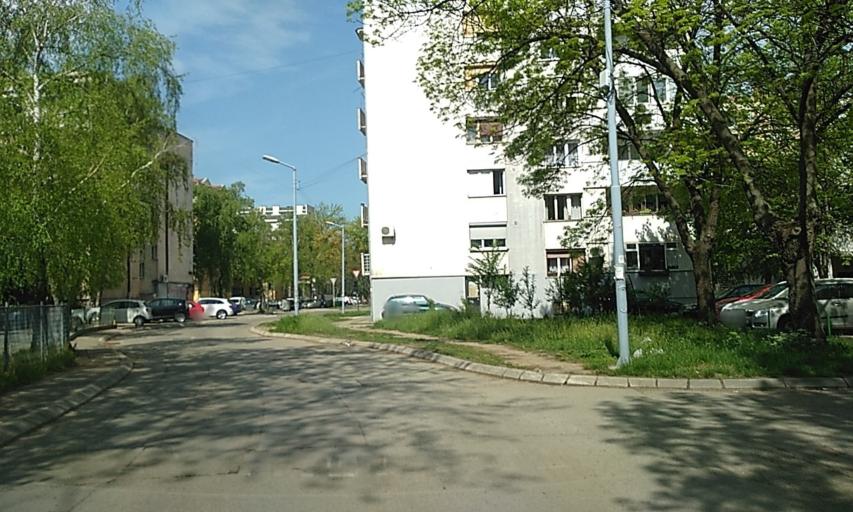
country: RS
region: Central Serbia
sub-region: Nisavski Okrug
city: Nis
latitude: 43.3181
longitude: 21.9201
